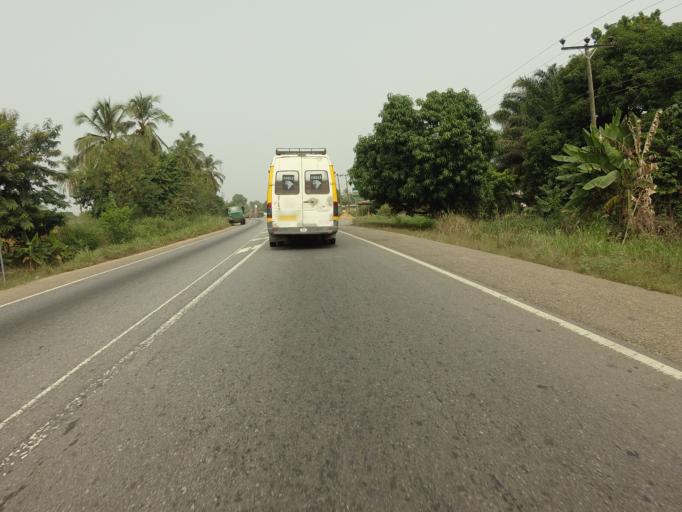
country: GH
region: Volta
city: Anloga
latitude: 6.0028
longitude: 0.5627
